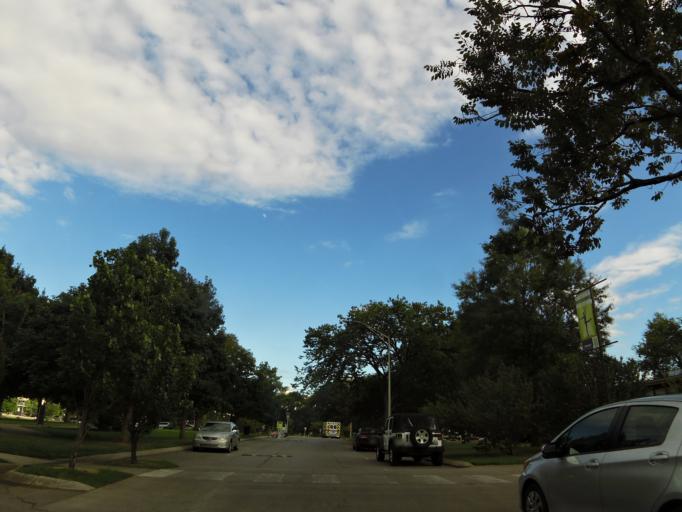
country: US
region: Tennessee
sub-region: Davidson County
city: Nashville
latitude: 36.1478
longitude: -86.8130
